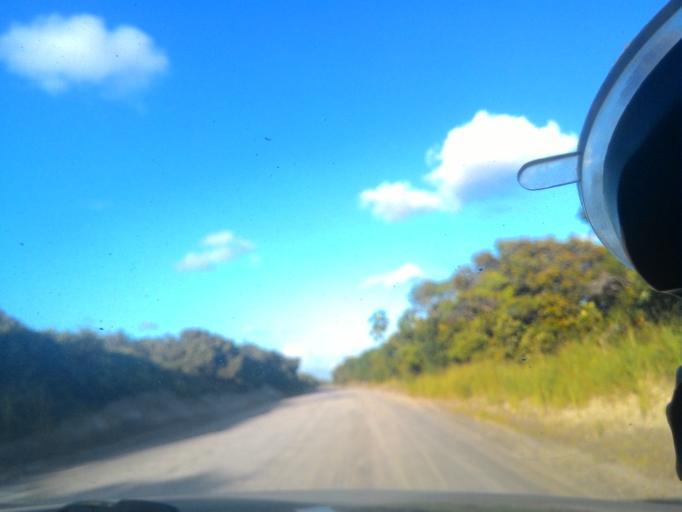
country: BR
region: Sao Paulo
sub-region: Pariquera-Acu
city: Pariquera Acu
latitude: -24.8831
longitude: -47.7400
